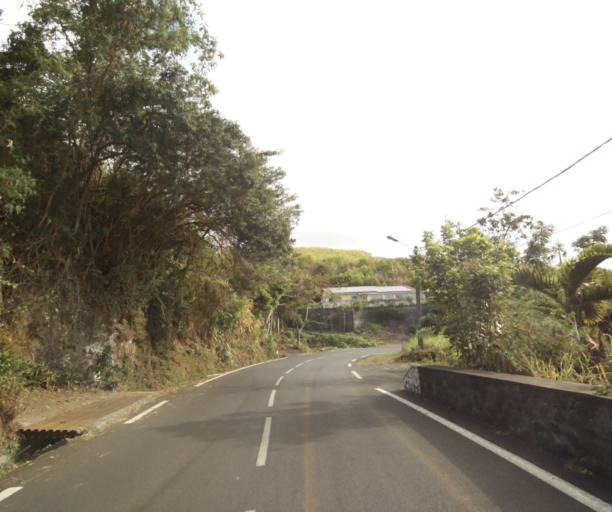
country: RE
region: Reunion
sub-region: Reunion
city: Saint-Paul
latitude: -21.0186
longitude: 55.3166
